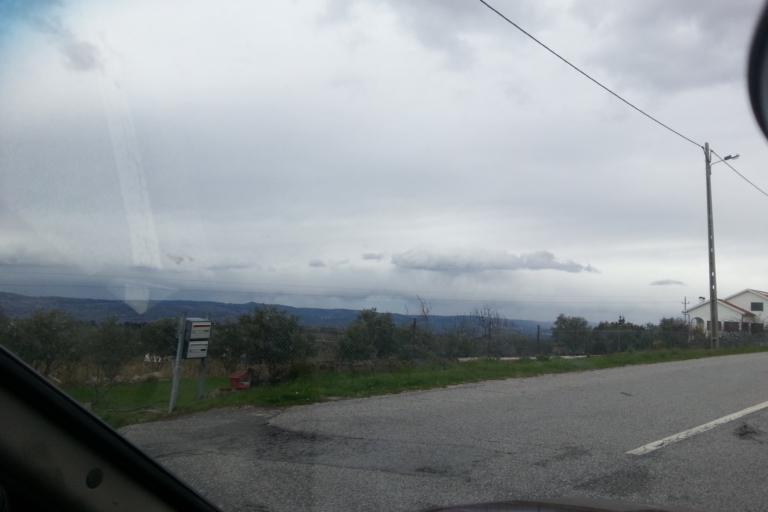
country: PT
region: Guarda
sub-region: Manteigas
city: Manteigas
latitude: 40.4983
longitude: -7.5958
